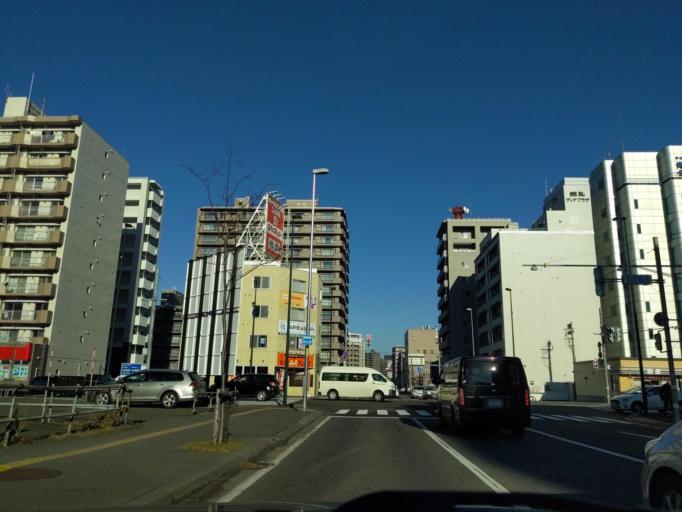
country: JP
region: Hokkaido
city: Sapporo
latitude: 43.0642
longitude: 141.3334
